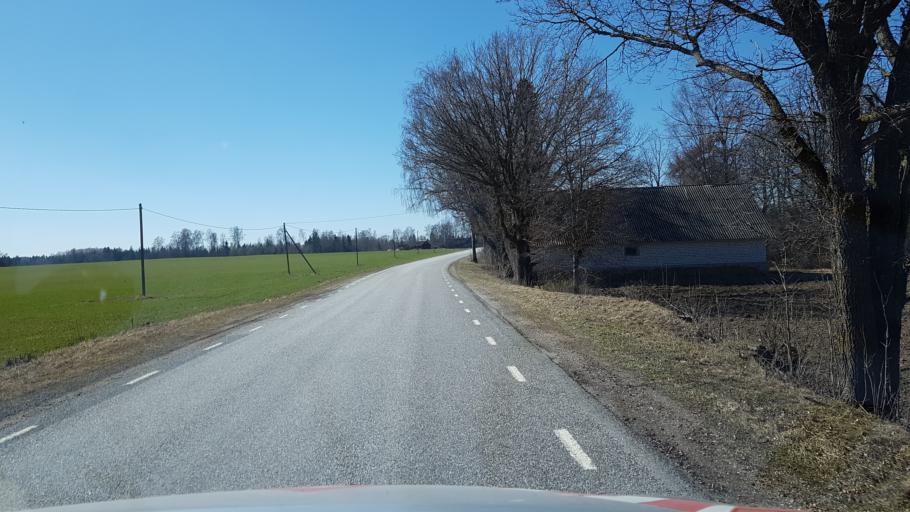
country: EE
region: Jaervamaa
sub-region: Koeru vald
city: Koeru
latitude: 59.0495
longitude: 26.0655
